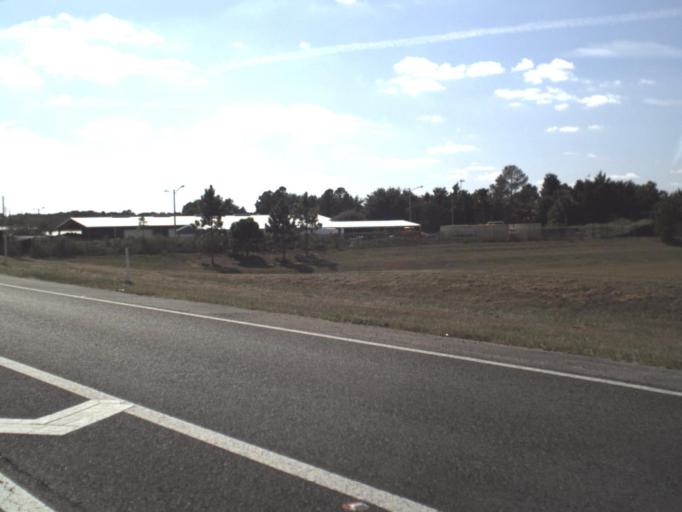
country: US
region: Florida
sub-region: Polk County
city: Citrus Ridge
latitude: 28.3707
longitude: -81.6101
